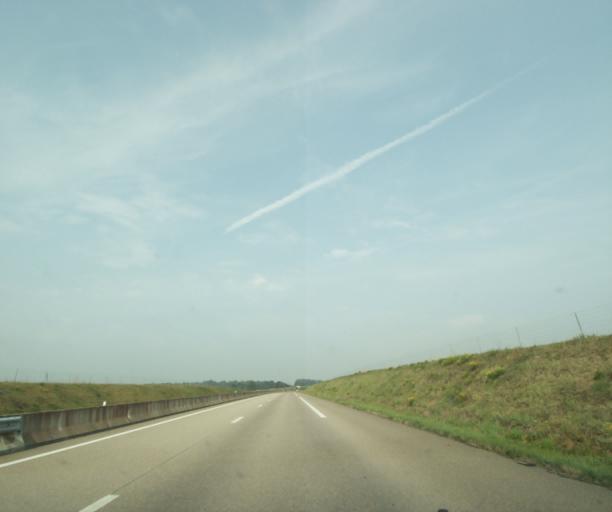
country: FR
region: Lower Normandy
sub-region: Departement de l'Orne
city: Ecouche
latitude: 48.7781
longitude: -0.1160
